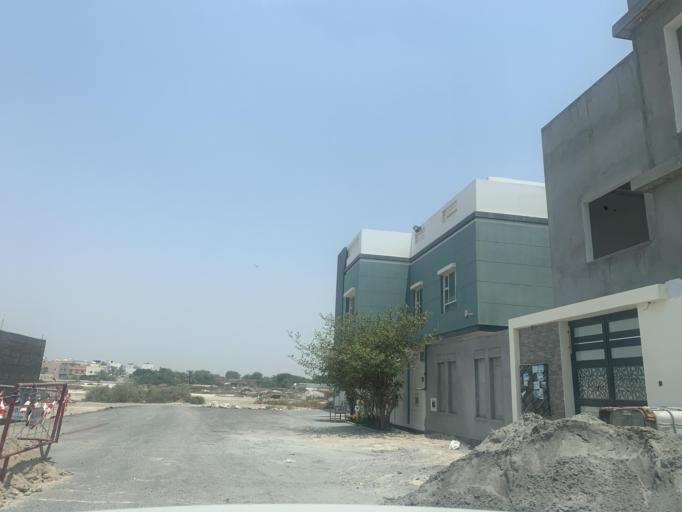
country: BH
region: Central Governorate
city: Madinat Hamad
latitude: 26.1403
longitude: 50.4631
